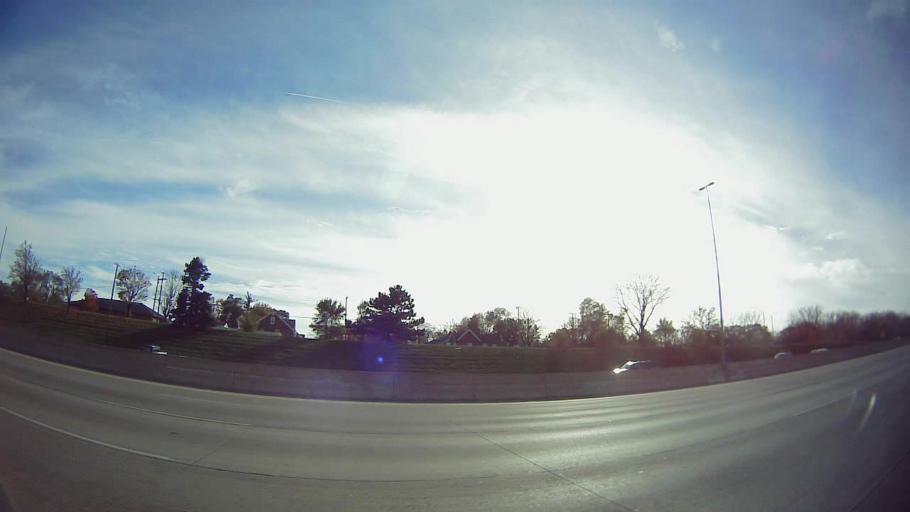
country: US
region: Michigan
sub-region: Wayne County
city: Redford
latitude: 42.3857
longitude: -83.2576
